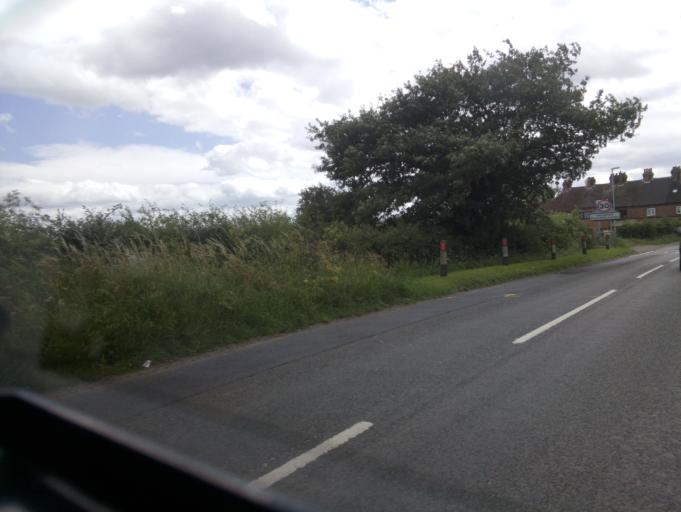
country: GB
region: England
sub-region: Nottinghamshire
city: West Bridgford
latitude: 52.9126
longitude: -1.0844
